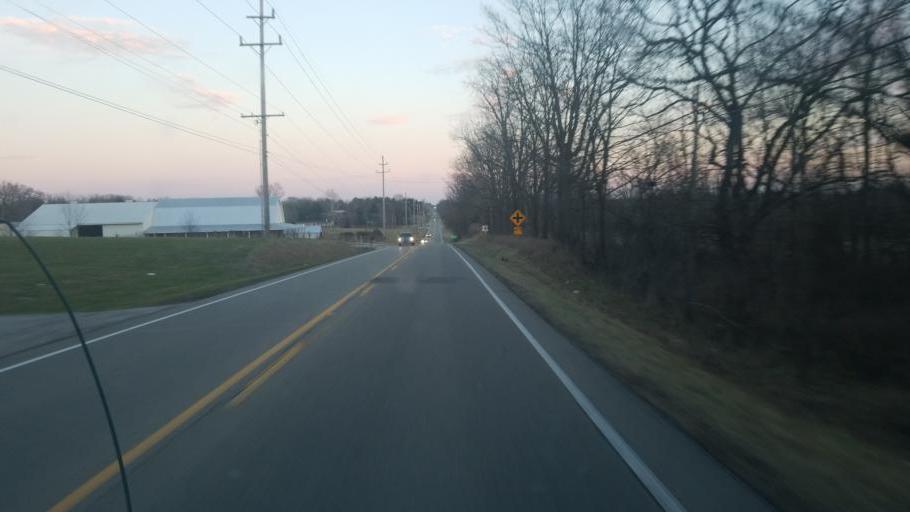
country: US
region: Indiana
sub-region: Lawrence County
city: Bedford
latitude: 38.8755
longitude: -86.4002
